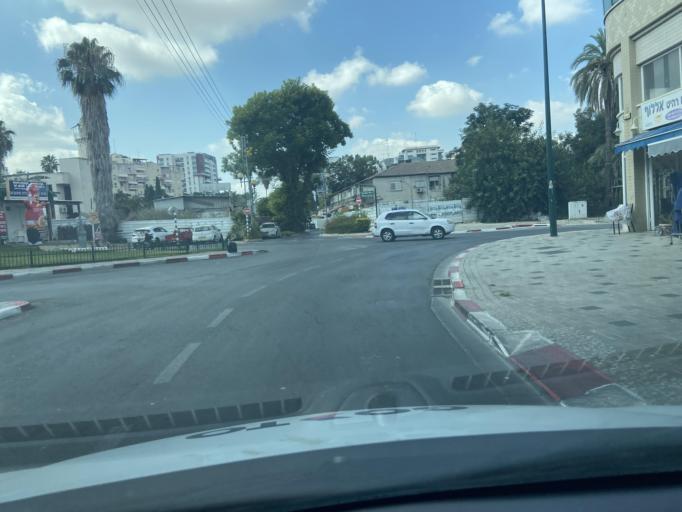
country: IL
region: Central District
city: Yehud
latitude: 32.0318
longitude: 34.8885
